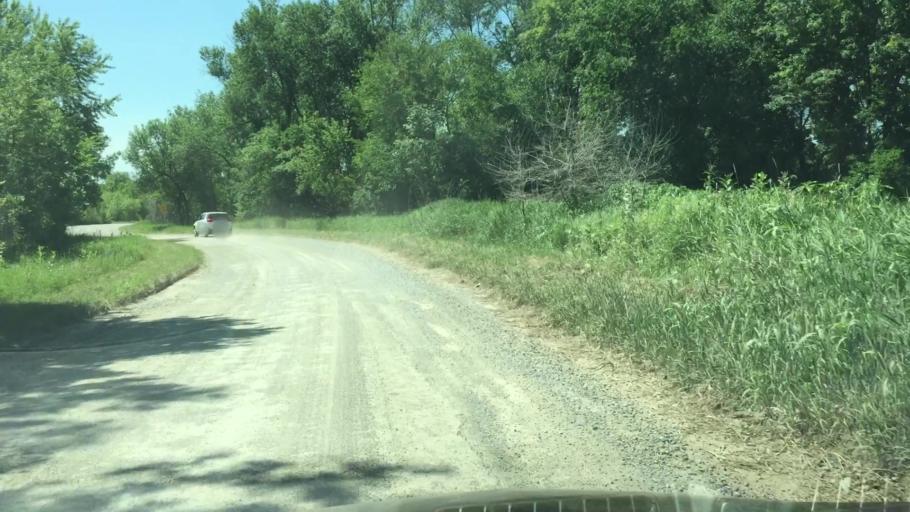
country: US
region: Iowa
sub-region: Linn County
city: Ely
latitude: 41.8190
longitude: -91.5894
